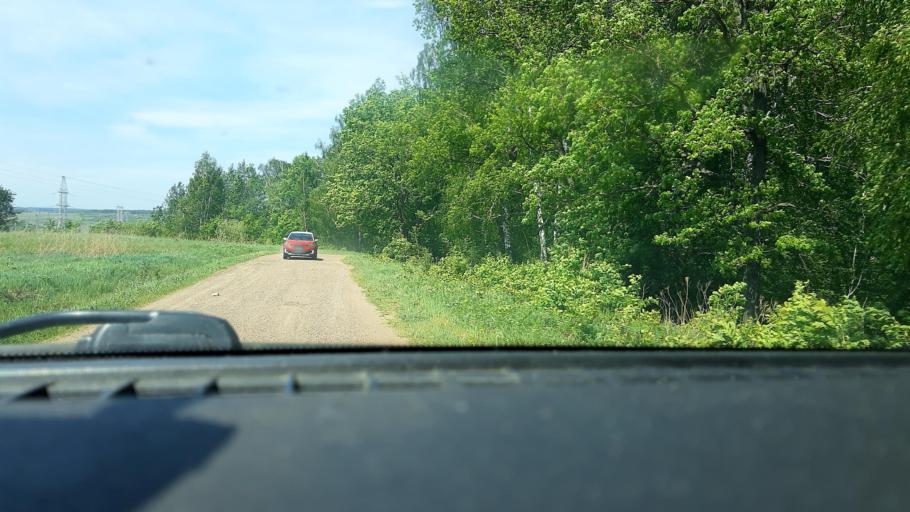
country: RU
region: Bashkortostan
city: Avdon
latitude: 54.4267
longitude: 55.8426
